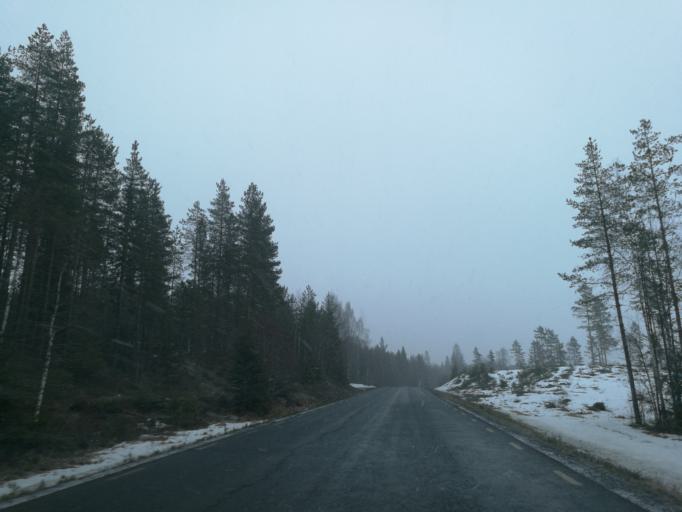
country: NO
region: Hedmark
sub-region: Grue
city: Kirkenaer
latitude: 60.6828
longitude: 12.6498
